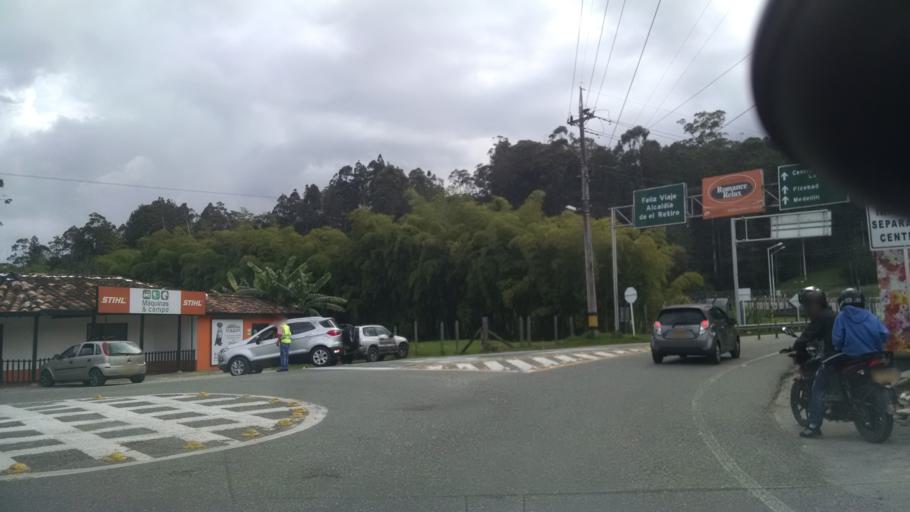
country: CO
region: Antioquia
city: El Retiro
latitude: 6.0943
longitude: -75.4899
